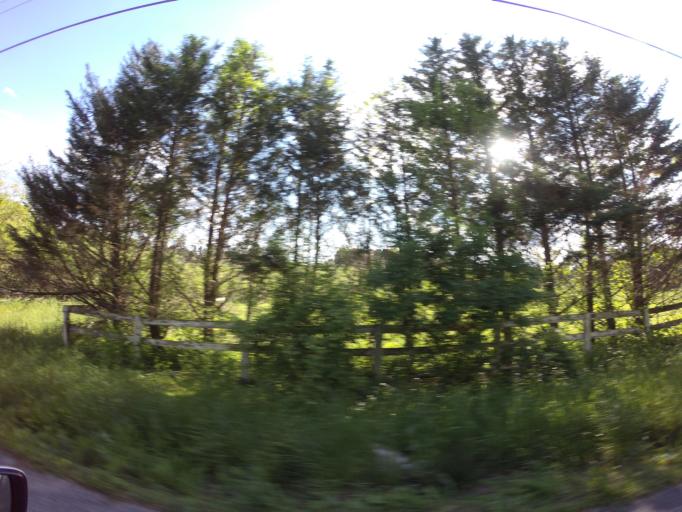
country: US
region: Maryland
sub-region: Baltimore County
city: Hunt Valley
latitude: 39.5182
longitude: -76.7187
